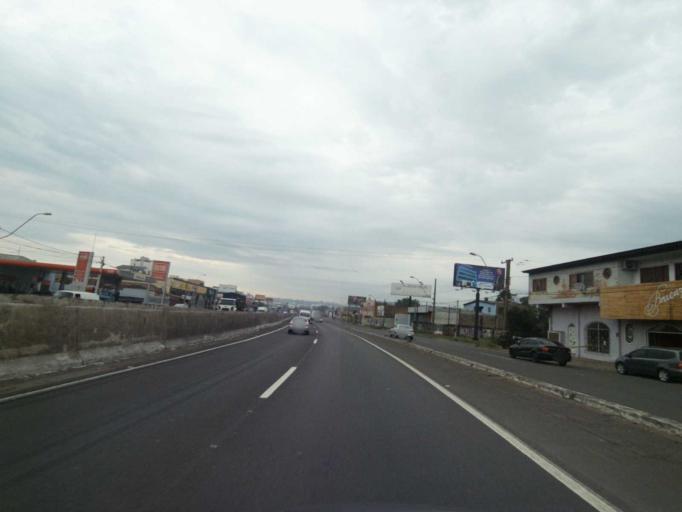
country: BR
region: Rio Grande do Sul
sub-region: Sao Leopoldo
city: Sao Leopoldo
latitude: -29.7655
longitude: -51.1541
